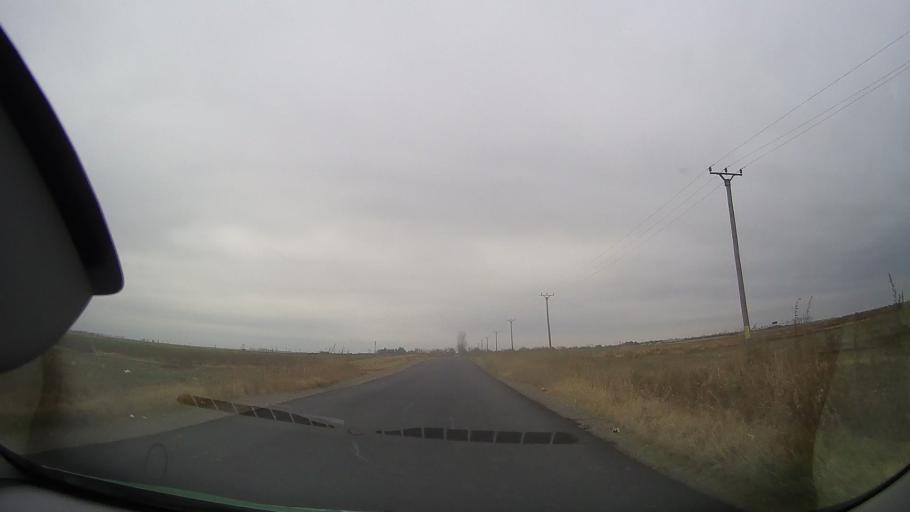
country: RO
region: Braila
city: Dudesti
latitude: 44.9417
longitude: 27.4074
